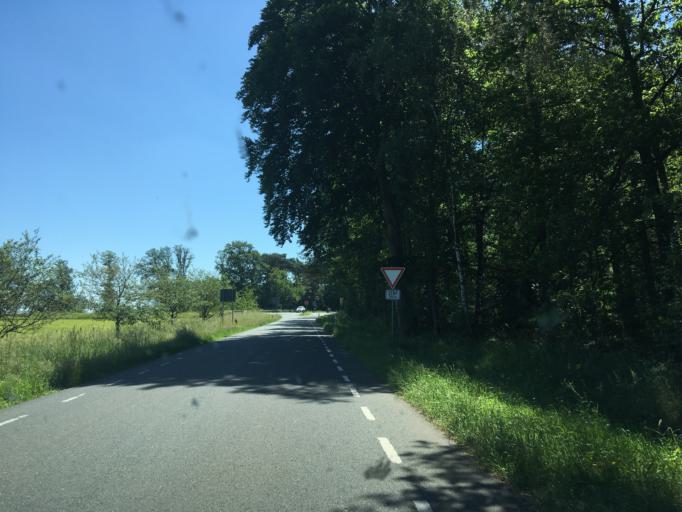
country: DE
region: North Rhine-Westphalia
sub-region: Regierungsbezirk Munster
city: Borken
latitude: 51.8169
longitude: 6.8118
